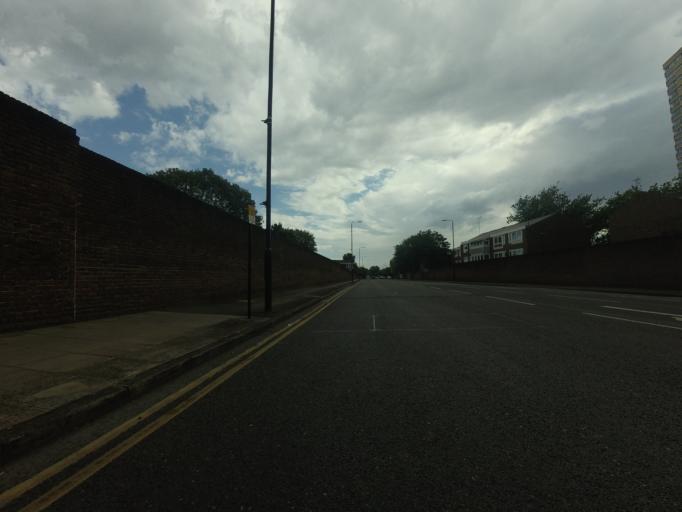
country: GB
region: England
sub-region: Greater London
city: Poplar
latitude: 51.5349
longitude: 0.0087
